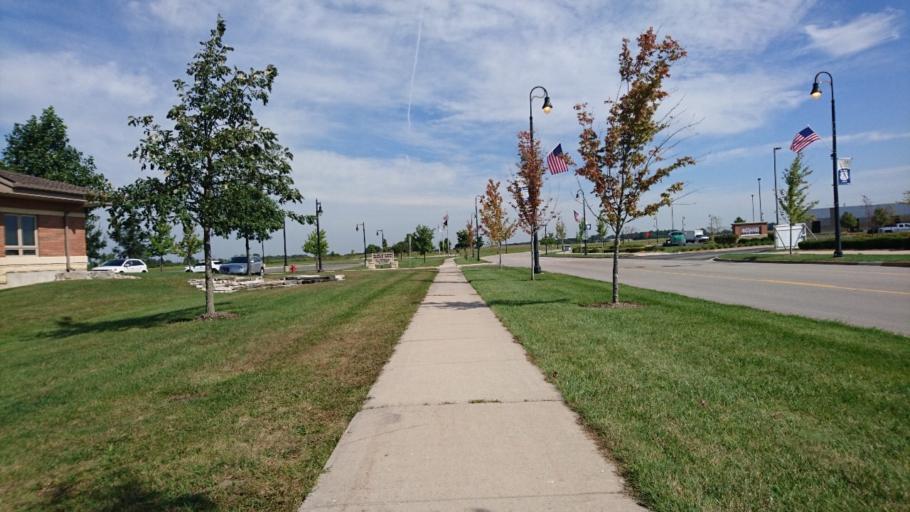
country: US
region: Illinois
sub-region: Will County
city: Elwood
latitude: 41.4052
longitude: -88.1056
